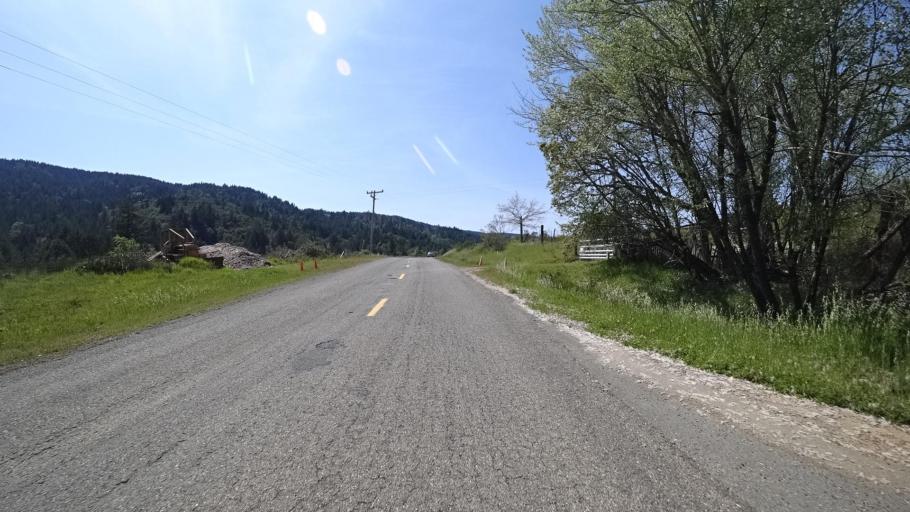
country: US
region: California
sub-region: Humboldt County
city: Redway
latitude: 40.3398
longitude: -123.7005
